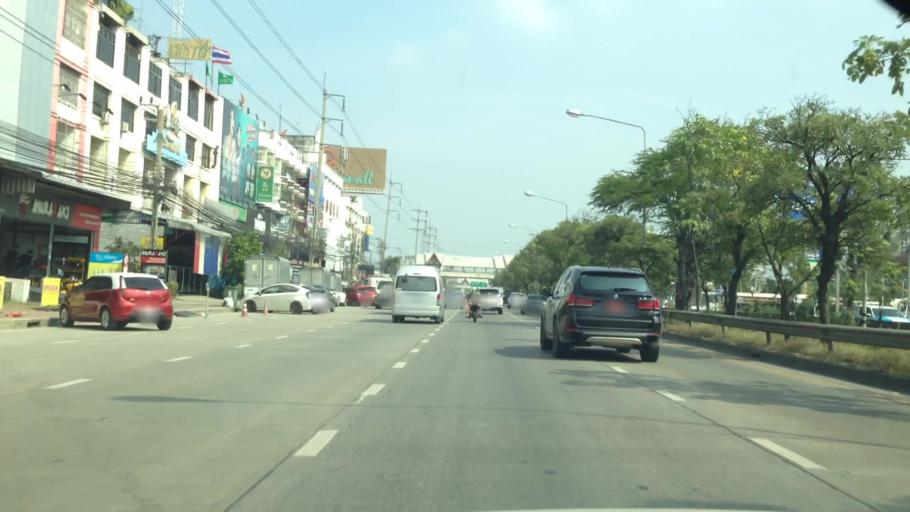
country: TH
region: Samut Prakan
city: Samut Prakan
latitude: 13.6180
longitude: 100.6219
